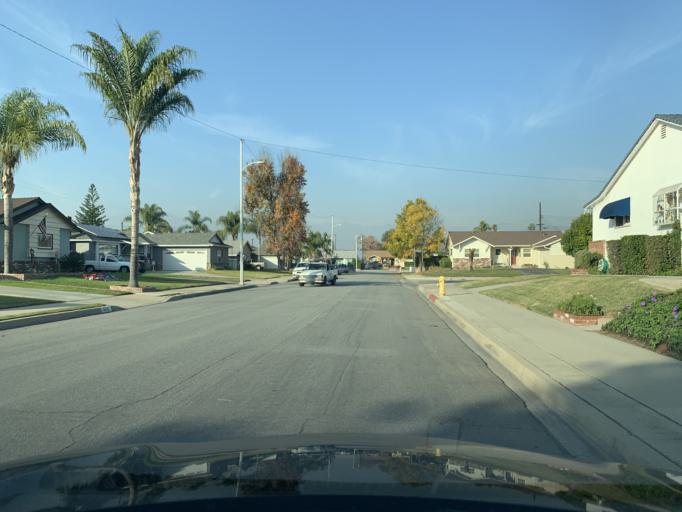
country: US
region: California
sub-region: Los Angeles County
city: Covina
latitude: 34.0904
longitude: -117.9000
